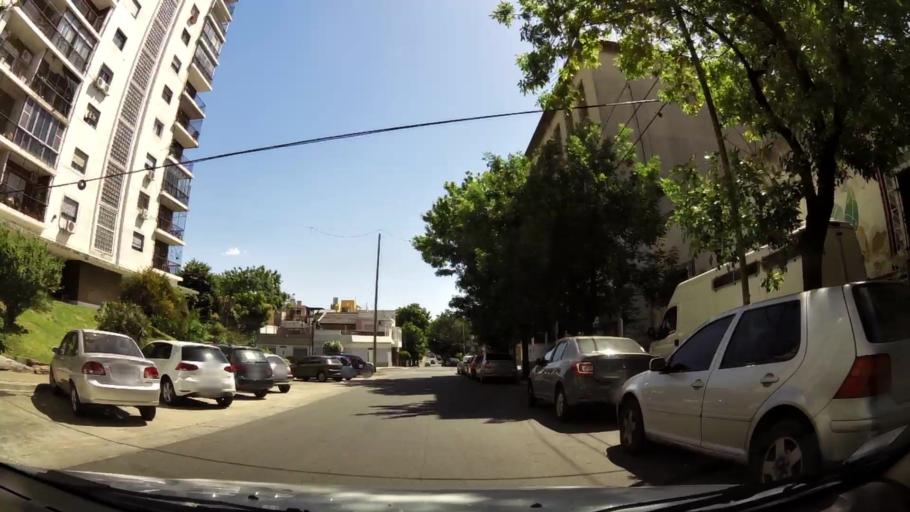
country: AR
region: Buenos Aires F.D.
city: Villa Santa Rita
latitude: -34.6337
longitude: -58.4503
